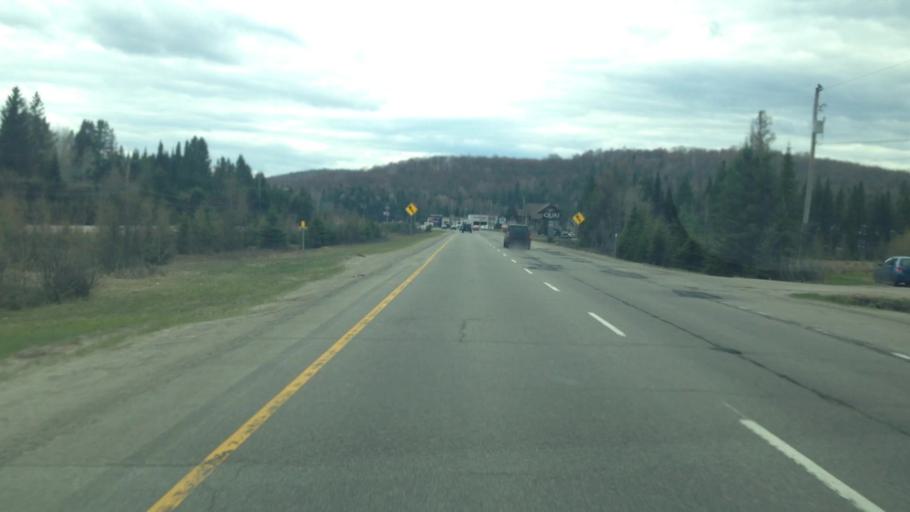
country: CA
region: Quebec
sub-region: Laurentides
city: Sainte-Agathe-des-Monts
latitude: 46.0734
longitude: -74.3147
